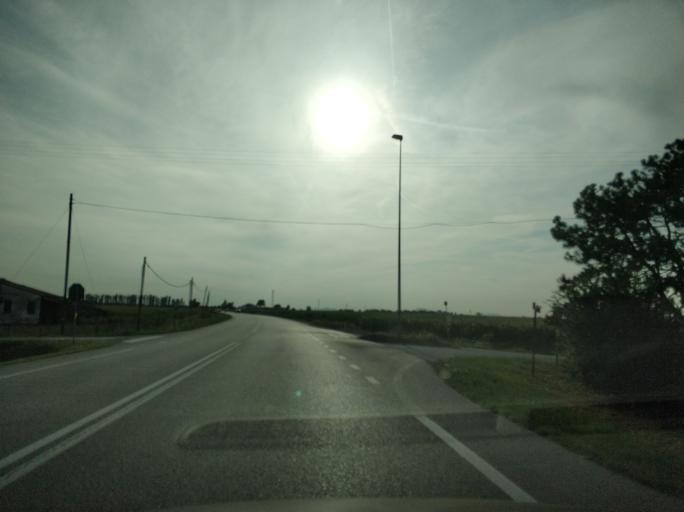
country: IT
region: Veneto
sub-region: Provincia di Padova
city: Correzzola
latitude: 45.2178
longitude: 12.0958
